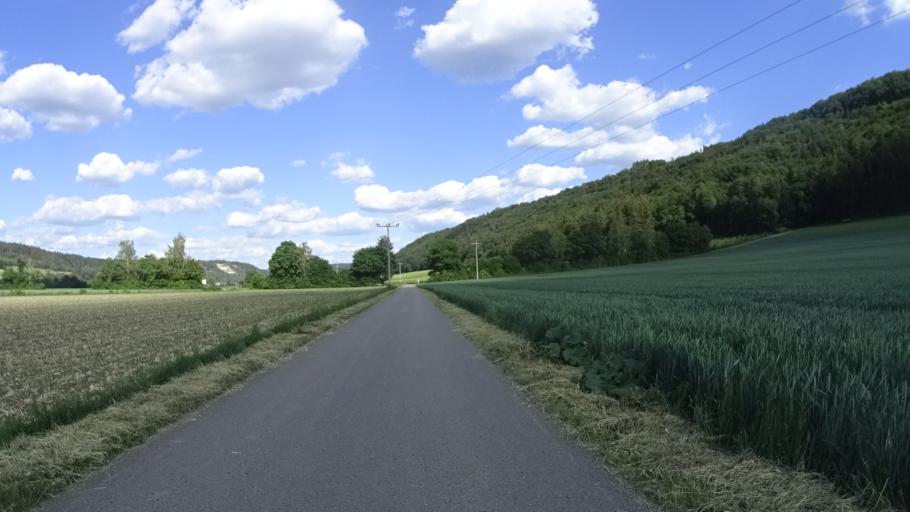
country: DE
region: Bavaria
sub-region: Upper Palatinate
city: Dietfurt
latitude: 49.0189
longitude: 11.4958
